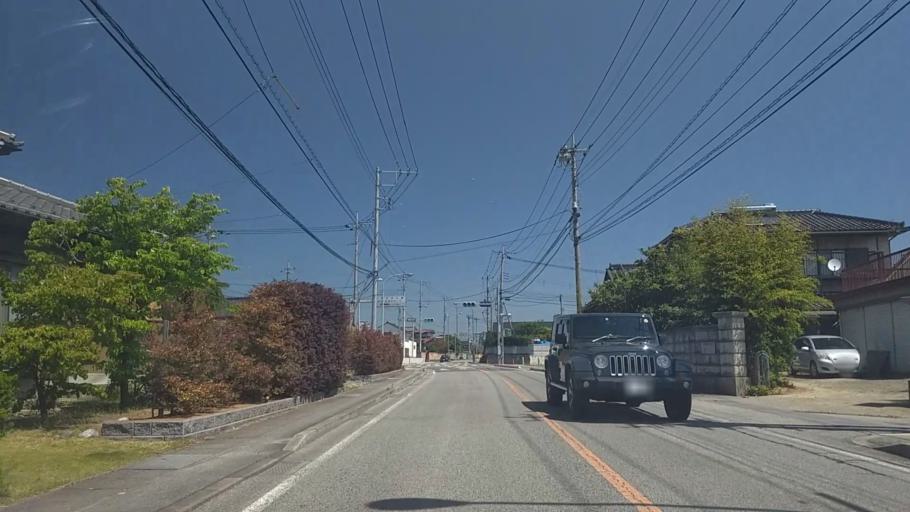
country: JP
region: Yamanashi
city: Ryuo
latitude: 35.6469
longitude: 138.4635
